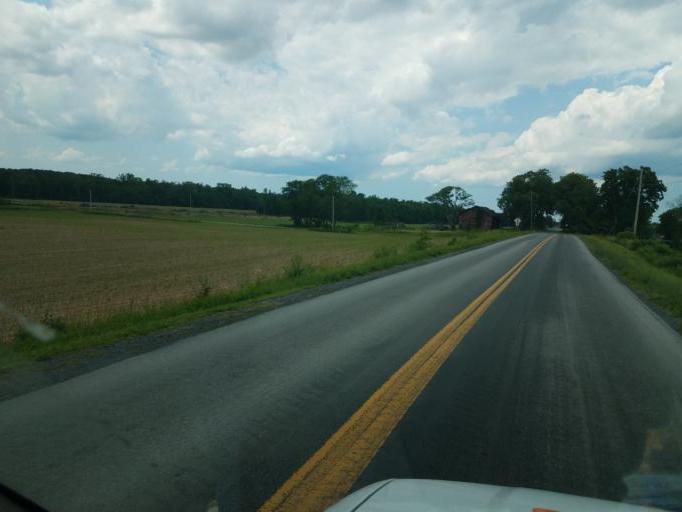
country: US
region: New York
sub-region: Wayne County
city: Clyde
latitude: 43.0161
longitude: -76.8783
